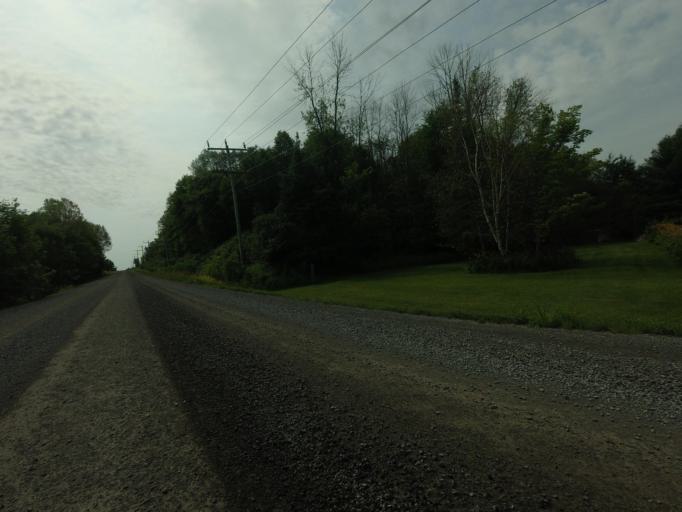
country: CA
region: Ontario
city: Arnprior
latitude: 45.4081
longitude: -76.2340
